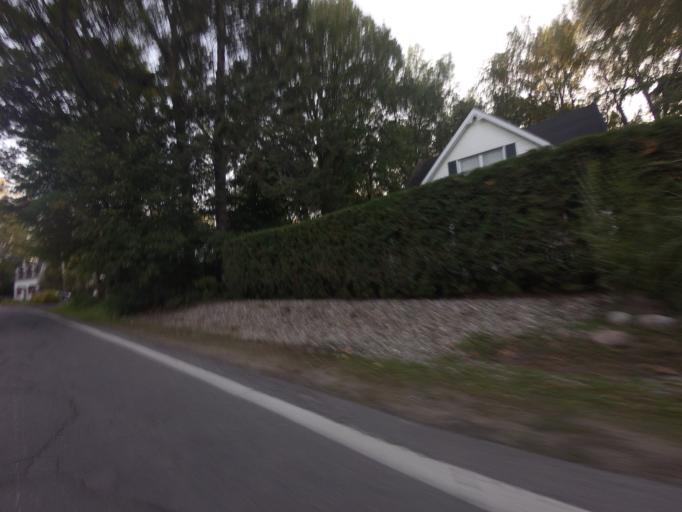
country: CA
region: Quebec
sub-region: Laurentides
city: Oka
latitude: 45.4494
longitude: -74.1100
